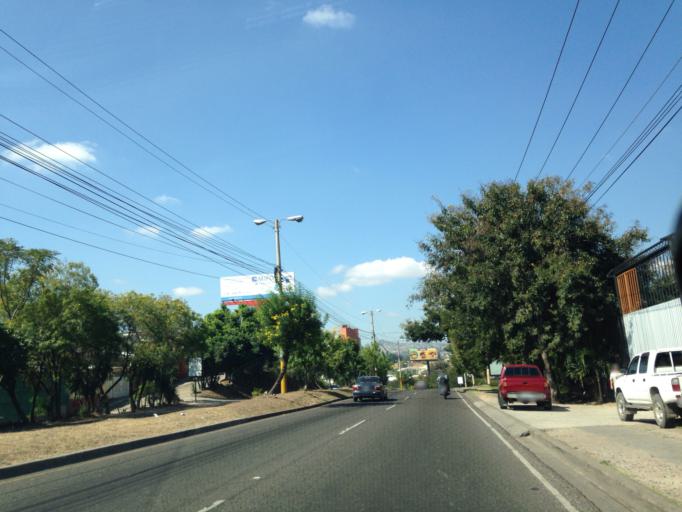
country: HN
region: Francisco Morazan
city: Tegucigalpa
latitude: 14.0763
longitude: -87.1953
